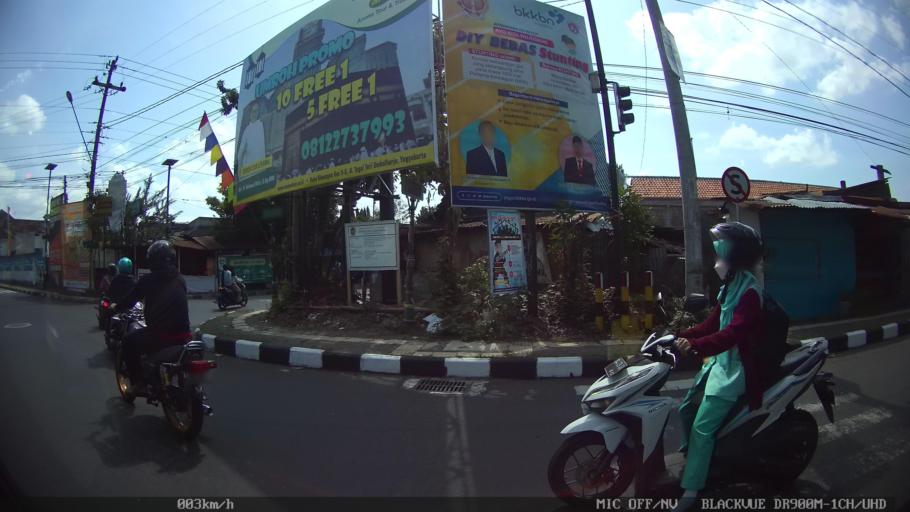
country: ID
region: Daerah Istimewa Yogyakarta
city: Yogyakarta
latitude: -7.8250
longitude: 110.3787
